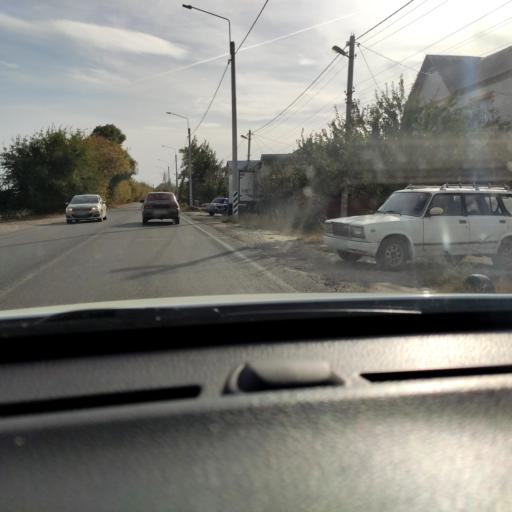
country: RU
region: Voronezj
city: Maslovka
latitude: 51.5645
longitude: 39.2455
